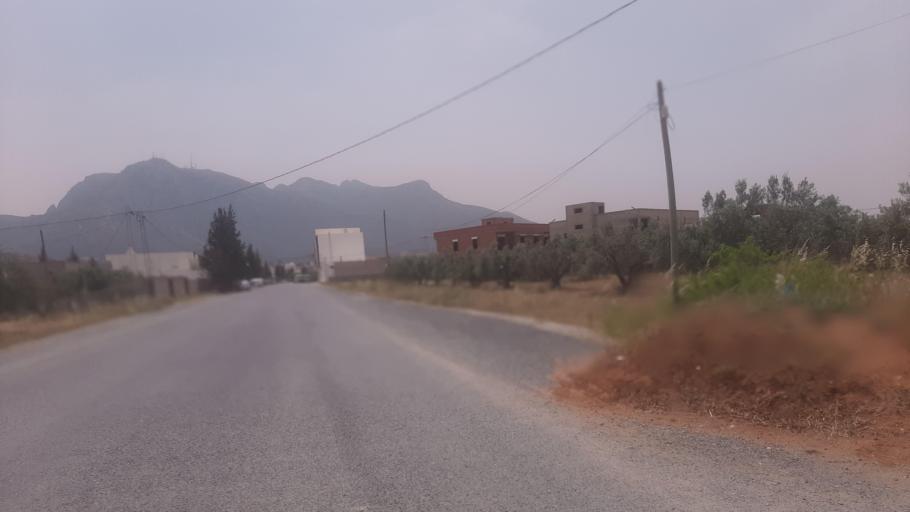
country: TN
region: Zaghwan
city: Zaghouan
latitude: 36.4162
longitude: 10.1360
